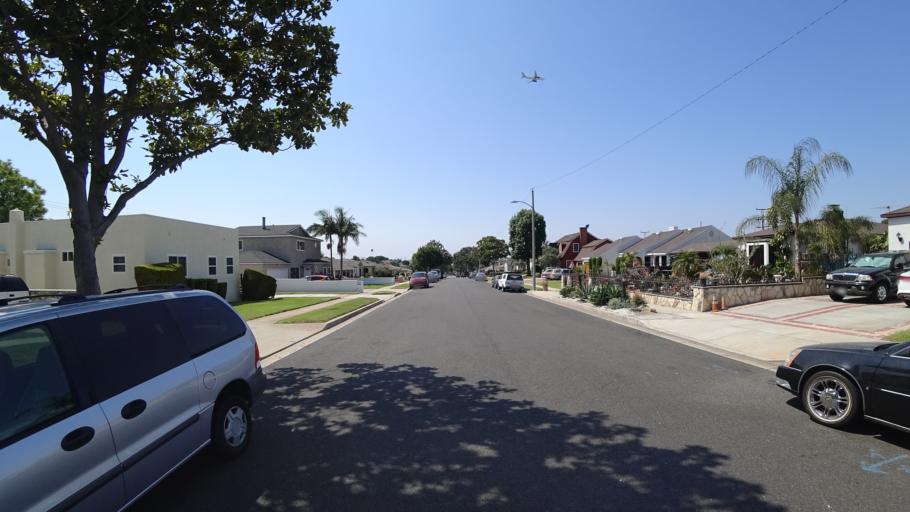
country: US
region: California
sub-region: Los Angeles County
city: Westmont
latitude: 33.9482
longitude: -118.3199
